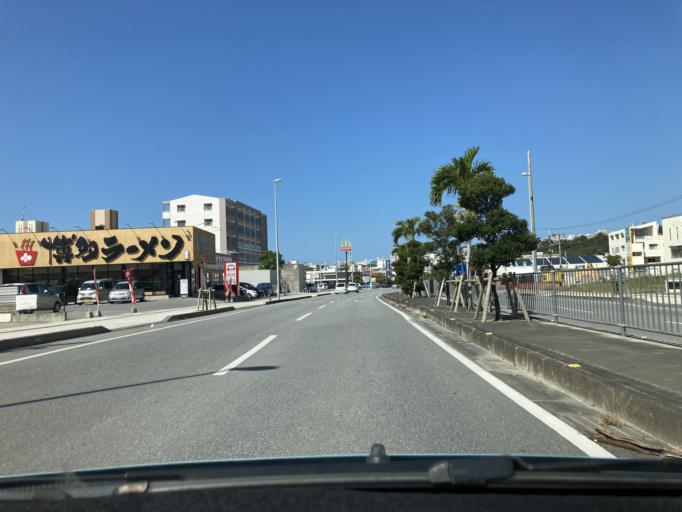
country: JP
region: Okinawa
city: Tomigusuku
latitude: 26.1911
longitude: 127.7150
